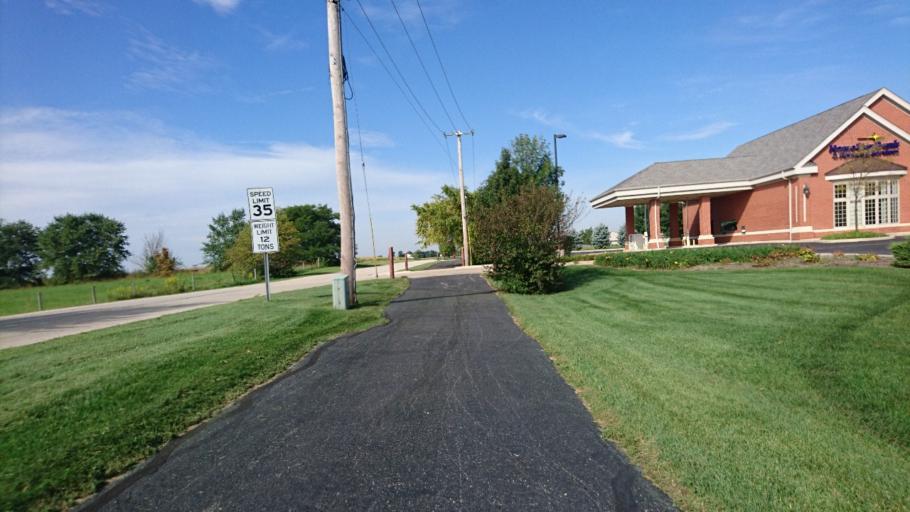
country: US
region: Illinois
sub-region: Will County
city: Manhattan
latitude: 41.4208
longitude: -88.0013
